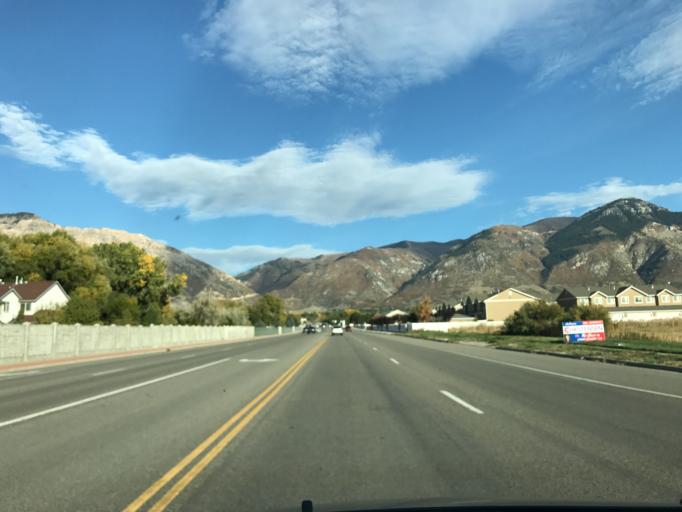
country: US
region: Utah
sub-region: Weber County
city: Pleasant View
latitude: 41.3055
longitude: -111.9852
